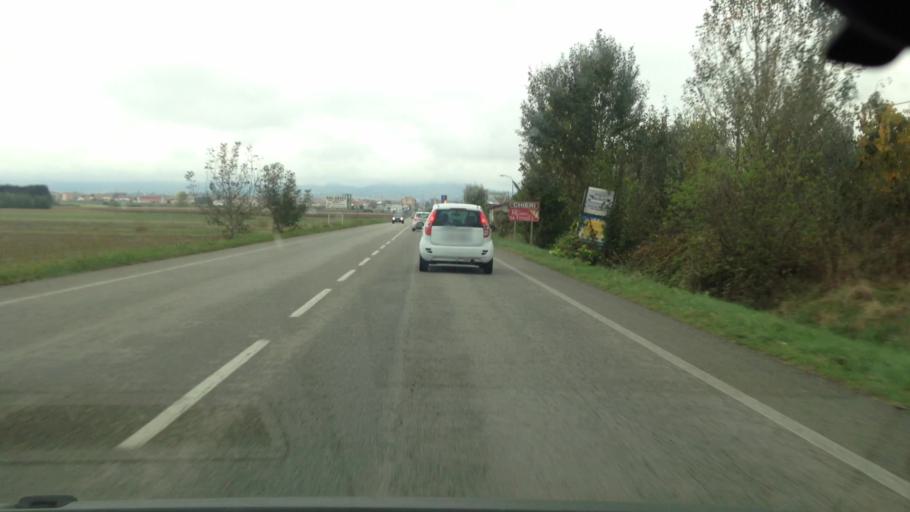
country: IT
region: Piedmont
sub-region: Provincia di Torino
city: Riva Presso Chieri
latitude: 44.9940
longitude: 7.8603
